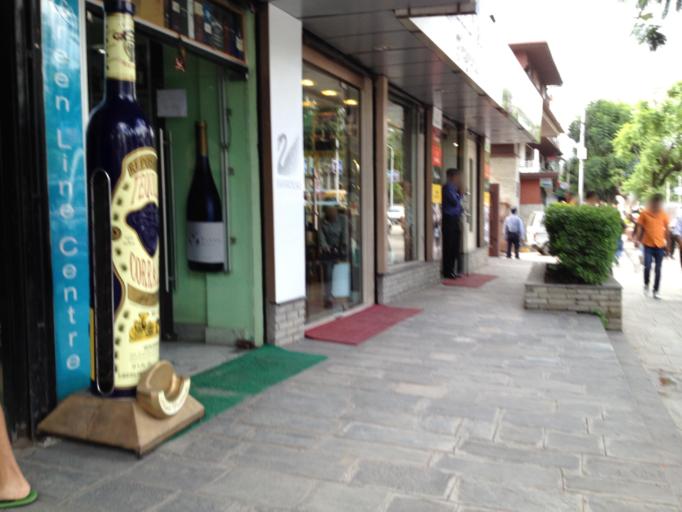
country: NP
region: Central Region
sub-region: Bagmati Zone
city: Kathmandu
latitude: 27.7108
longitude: 85.3176
